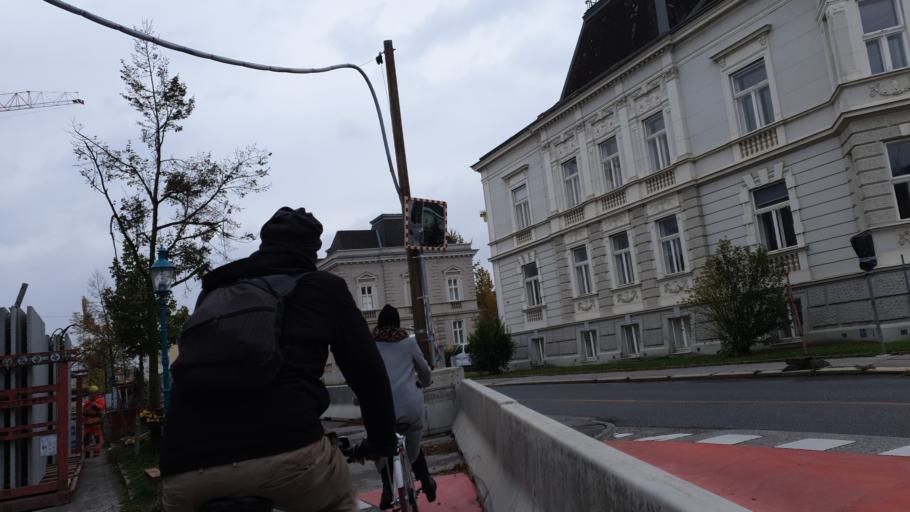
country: AT
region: Lower Austria
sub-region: Sankt Polten Stadt
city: Sankt Poelten
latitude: 48.2037
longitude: 15.6204
